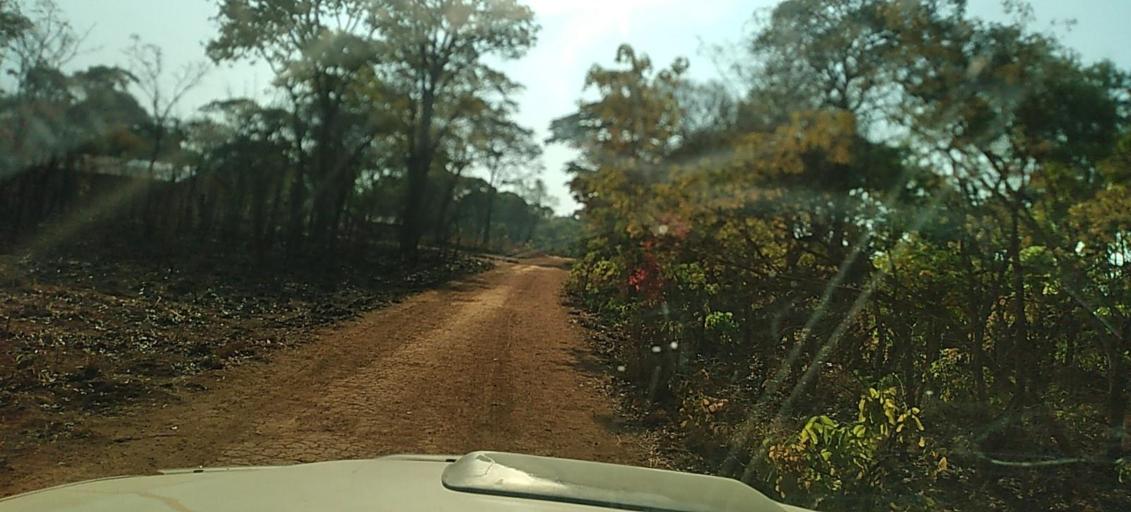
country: ZM
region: North-Western
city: Kasempa
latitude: -13.1852
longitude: 25.9598
